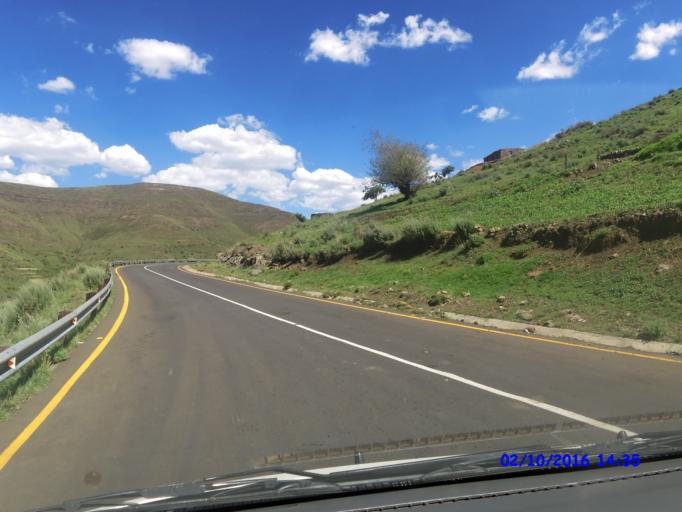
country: LS
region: Maseru
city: Nako
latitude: -29.4945
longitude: 28.0613
